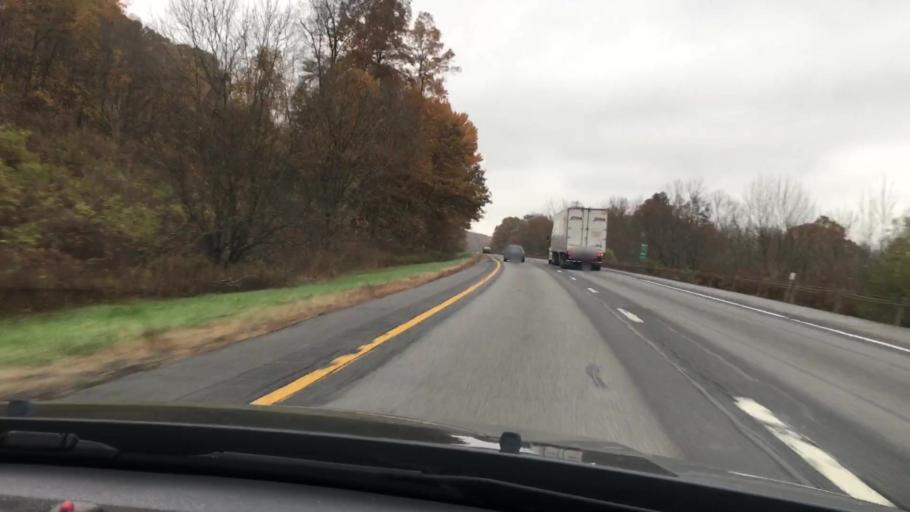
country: US
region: New York
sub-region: Putnam County
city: Lake Carmel
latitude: 41.4846
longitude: -73.6563
